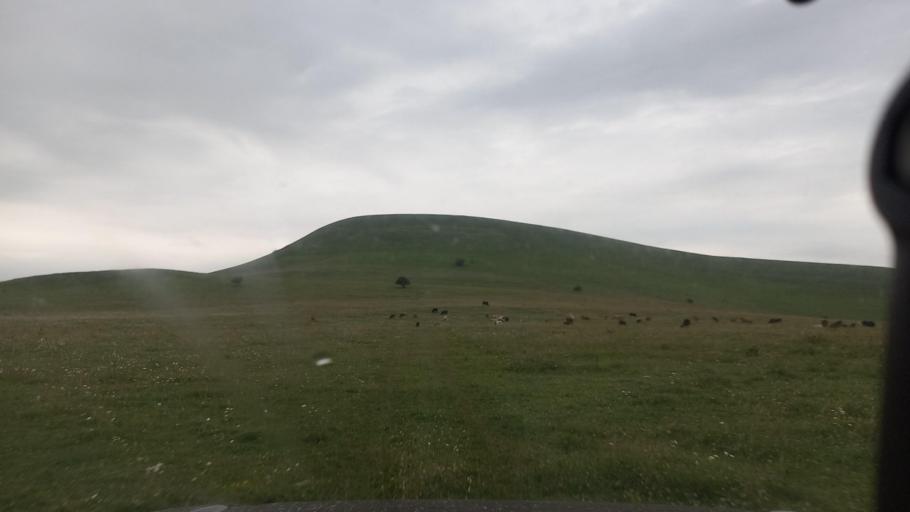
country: RU
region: Karachayevo-Cherkesiya
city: Pregradnaya
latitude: 43.9504
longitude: 41.1612
